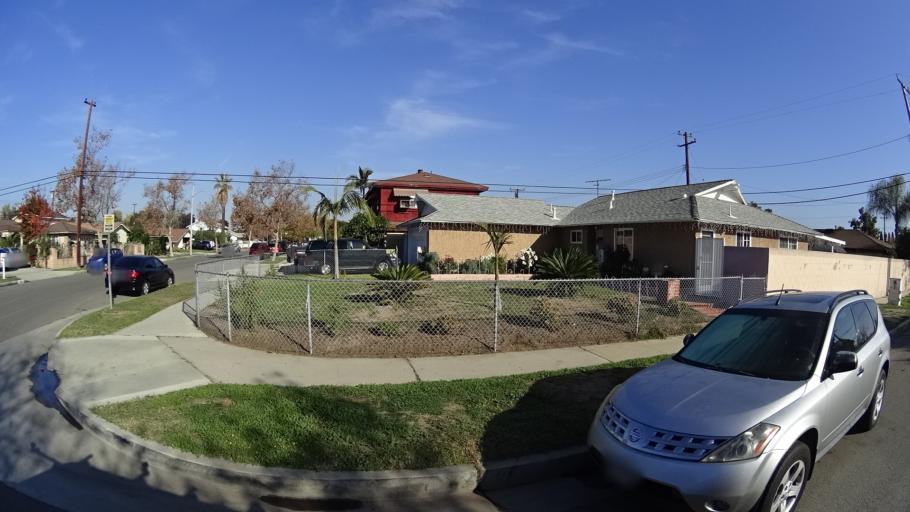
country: US
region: California
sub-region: Orange County
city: Fountain Valley
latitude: 33.7280
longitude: -117.9123
